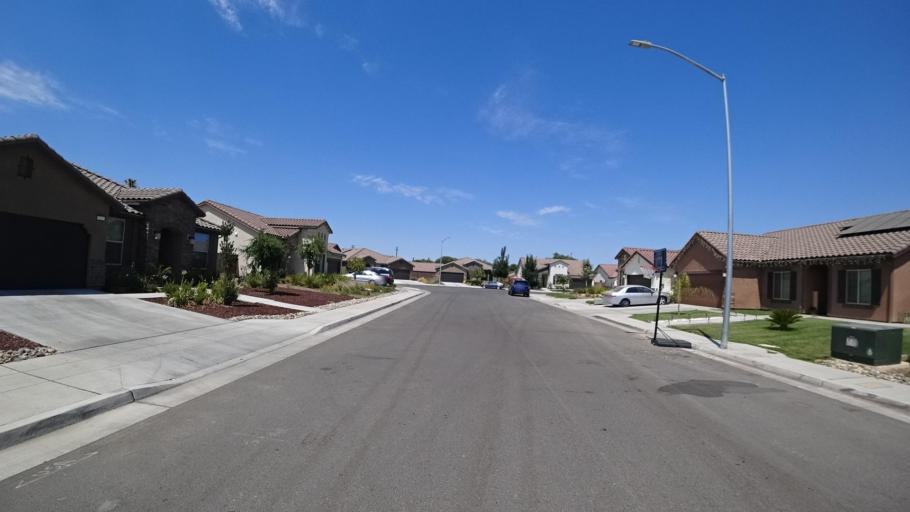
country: US
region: California
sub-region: Fresno County
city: Sunnyside
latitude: 36.7292
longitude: -119.7124
